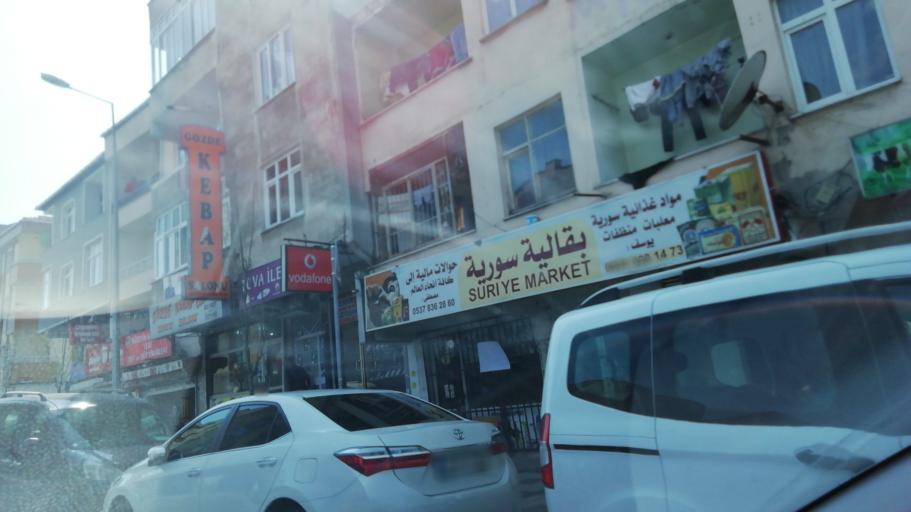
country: TR
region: Istanbul
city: Mahmutbey
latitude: 41.0355
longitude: 28.8199
